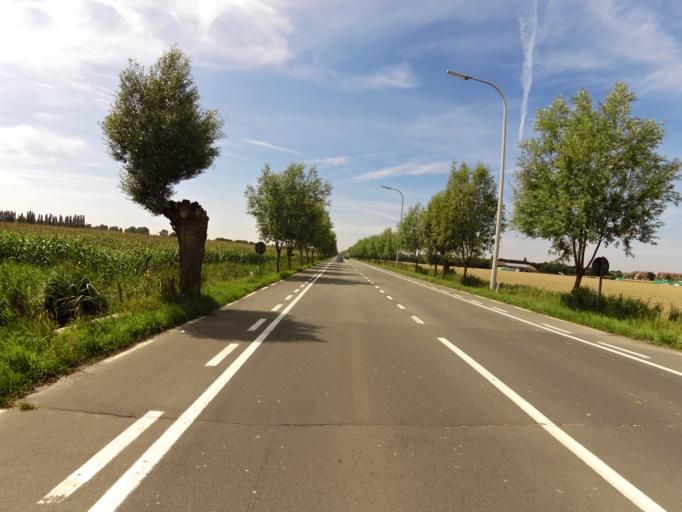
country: BE
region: Flanders
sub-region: Provincie West-Vlaanderen
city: Knokke-Heist
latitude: 51.3181
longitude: 3.3160
